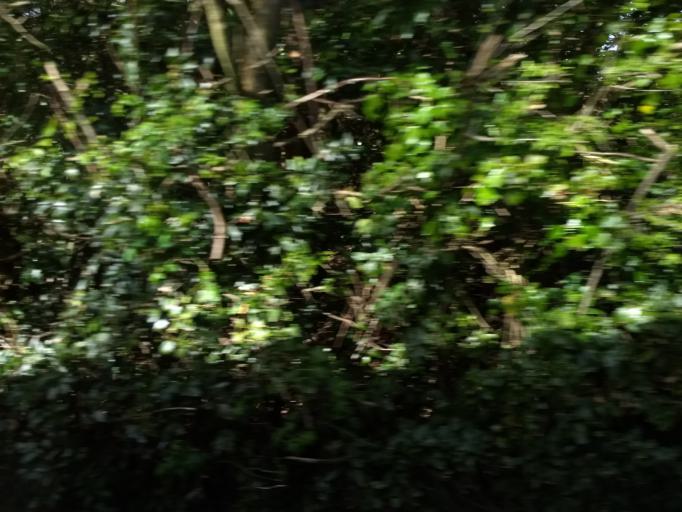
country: GB
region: England
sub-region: Isle of Wight
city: Seaview
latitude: 50.7190
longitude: -1.1304
